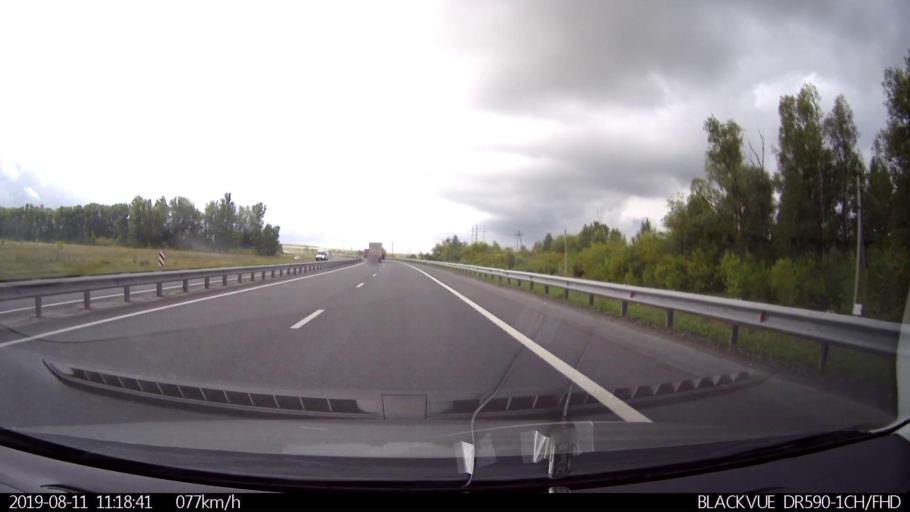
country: RU
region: Ulyanovsk
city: Novoul'yanovsk
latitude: 54.1776
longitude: 48.2659
